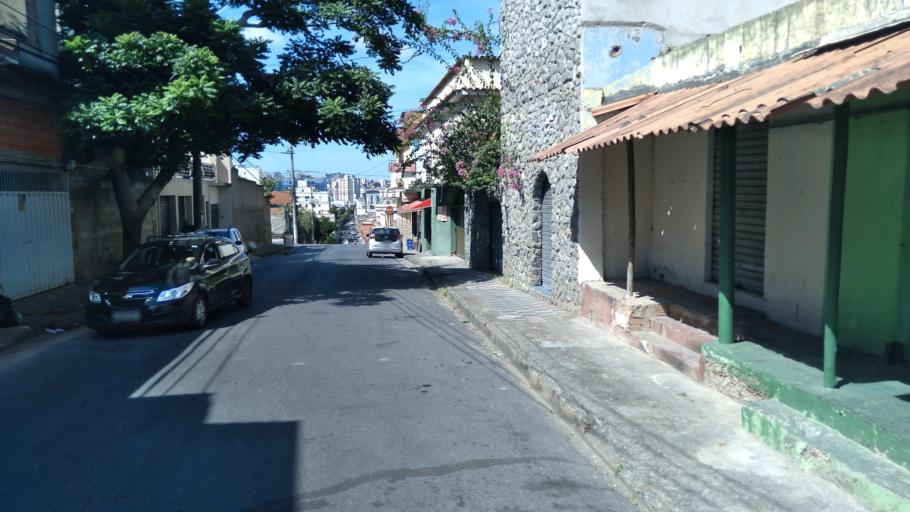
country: BR
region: Minas Gerais
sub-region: Belo Horizonte
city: Belo Horizonte
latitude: -19.8785
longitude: -43.9226
